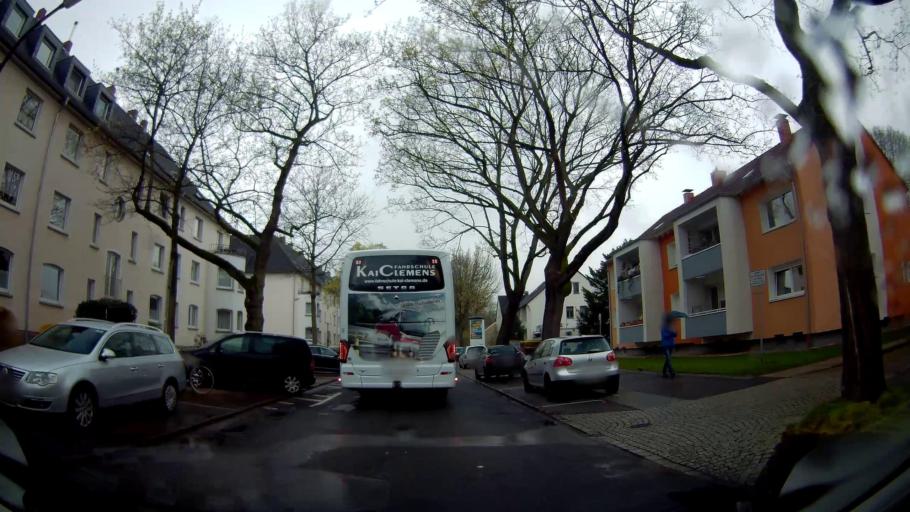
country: DE
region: North Rhine-Westphalia
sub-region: Regierungsbezirk Arnsberg
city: Dortmund
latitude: 51.5104
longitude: 7.5002
